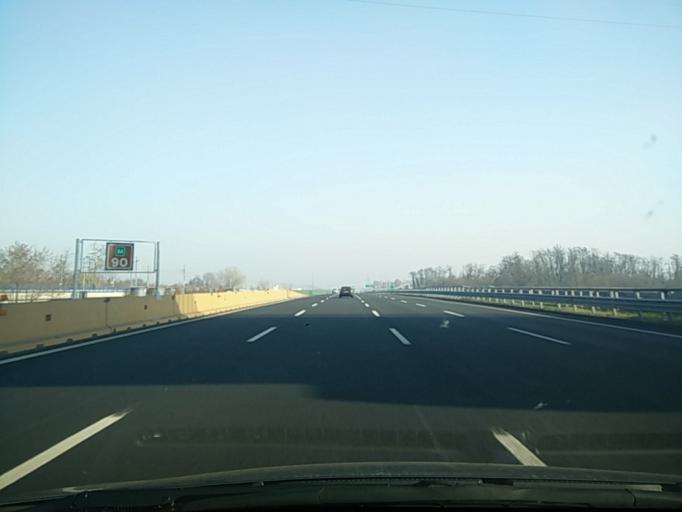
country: IT
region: Lombardy
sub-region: Citta metropolitana di Milano
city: Cornaredo
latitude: 45.5089
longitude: 9.0302
